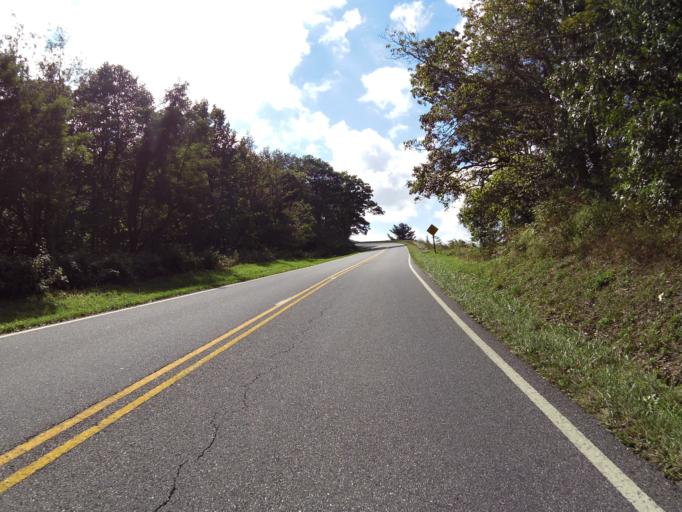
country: US
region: Virginia
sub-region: Page County
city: Luray
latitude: 38.6096
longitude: -78.3645
